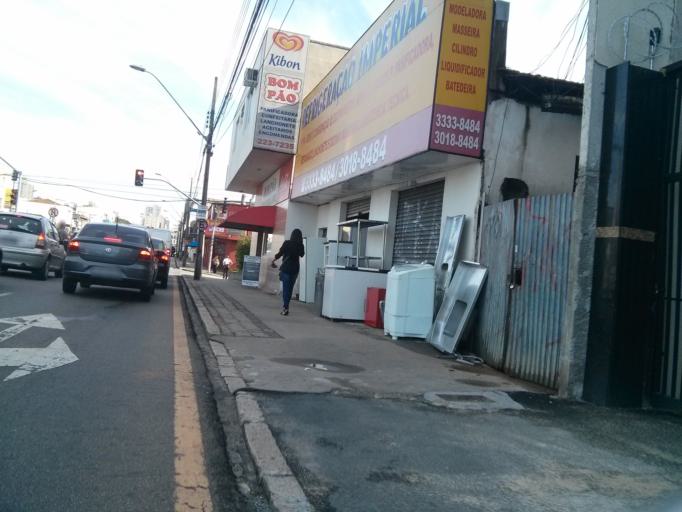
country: BR
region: Parana
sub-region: Curitiba
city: Curitiba
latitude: -25.4471
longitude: -49.2639
